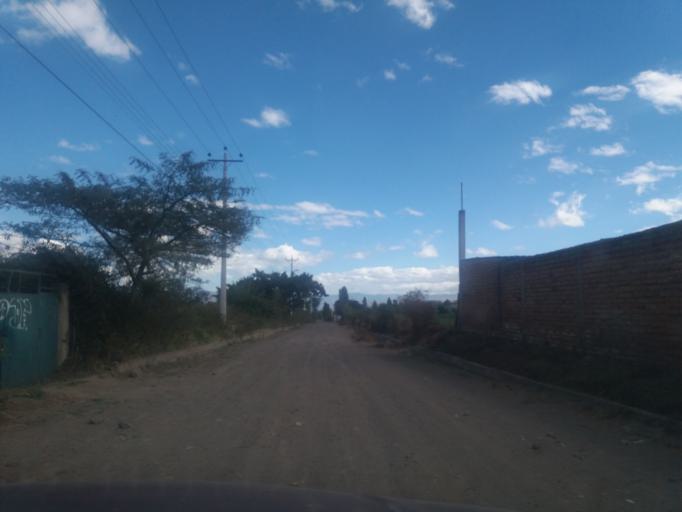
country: EC
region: Pichincha
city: Sangolqui
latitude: -0.1813
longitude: -78.3364
